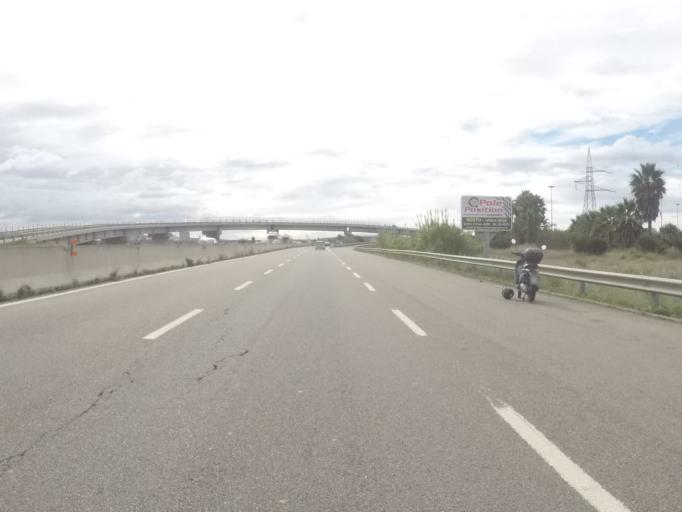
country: IT
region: Sardinia
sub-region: Provincia di Cagliari
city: Cagliari
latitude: 39.2215
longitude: 9.0827
